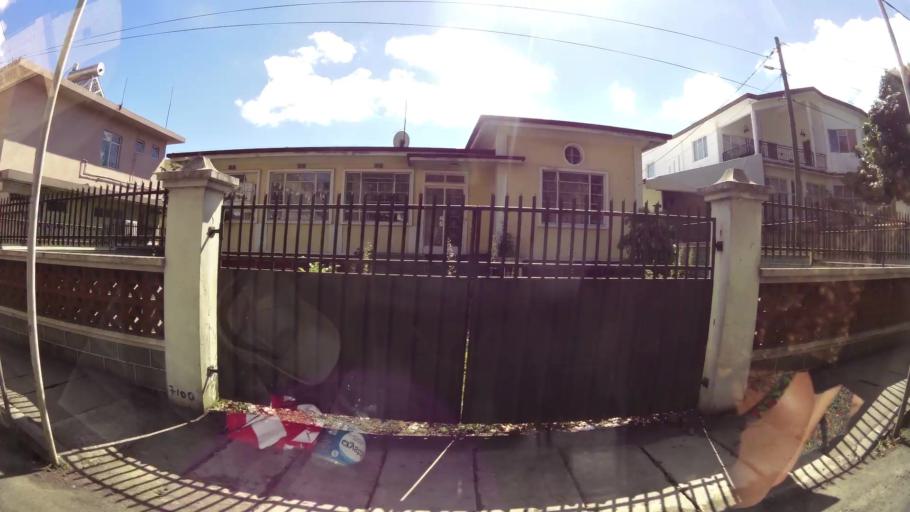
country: MU
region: Plaines Wilhems
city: Vacoas
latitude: -20.2998
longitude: 57.4907
